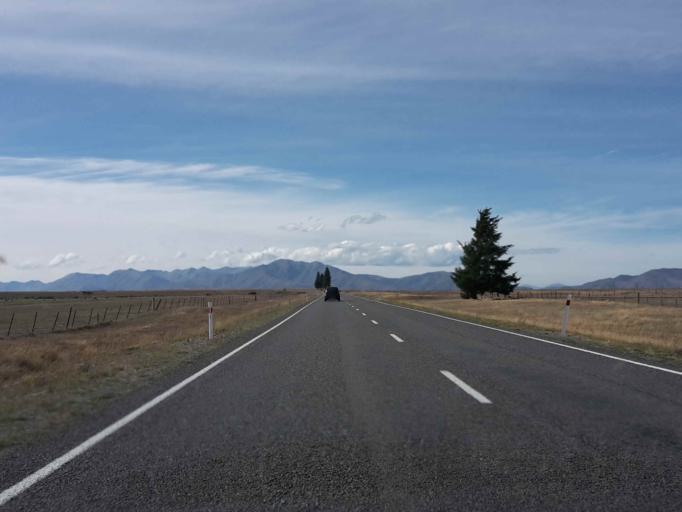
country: NZ
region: Canterbury
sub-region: Timaru District
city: Pleasant Point
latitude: -44.1733
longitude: 170.3259
